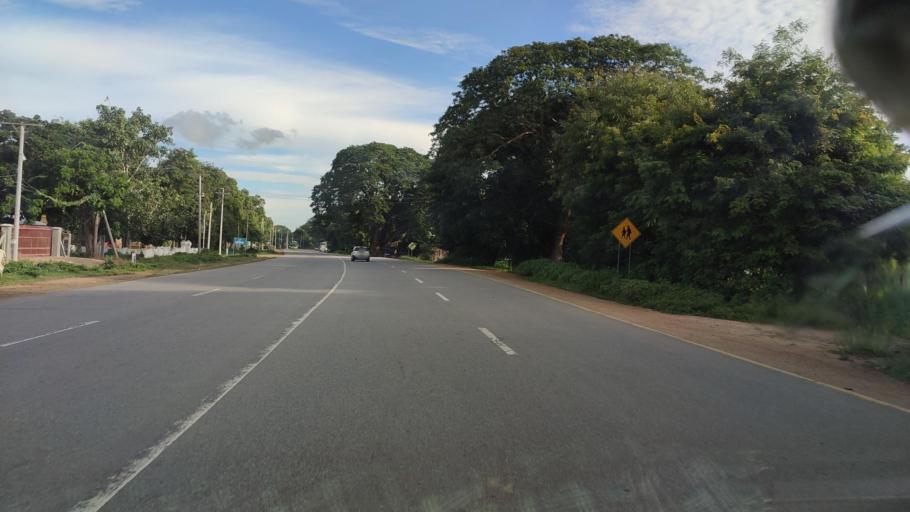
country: MM
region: Mandalay
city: Yamethin
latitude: 20.1802
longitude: 96.1884
